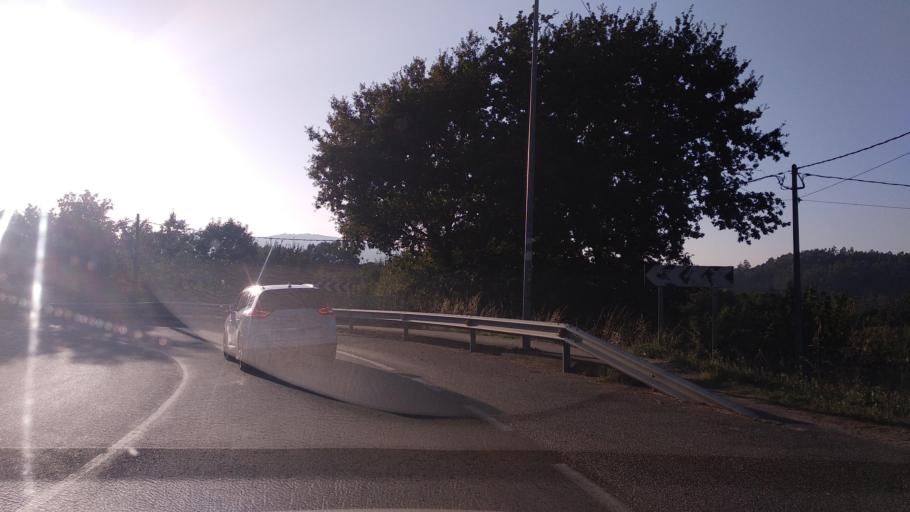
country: ES
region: Galicia
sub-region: Provincia de Pontevedra
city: Redondela
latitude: 42.3413
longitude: -8.5935
